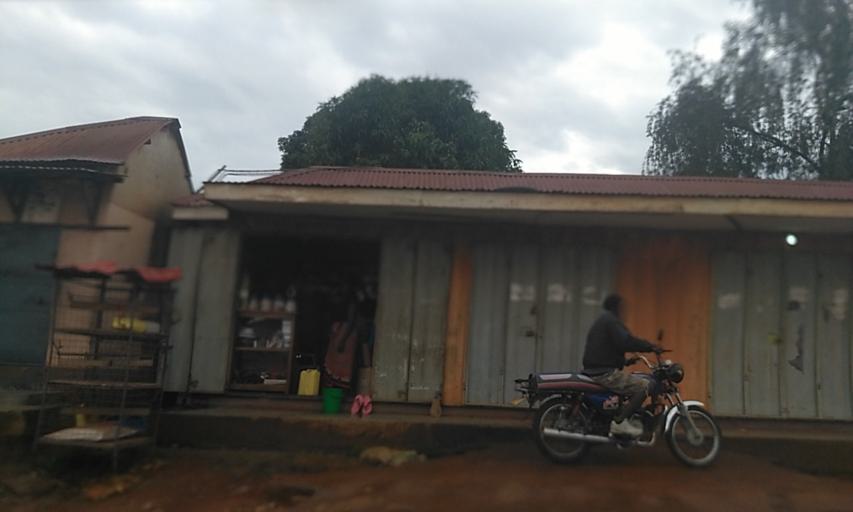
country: UG
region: Central Region
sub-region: Wakiso District
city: Bweyogerere
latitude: 0.3555
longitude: 32.6649
